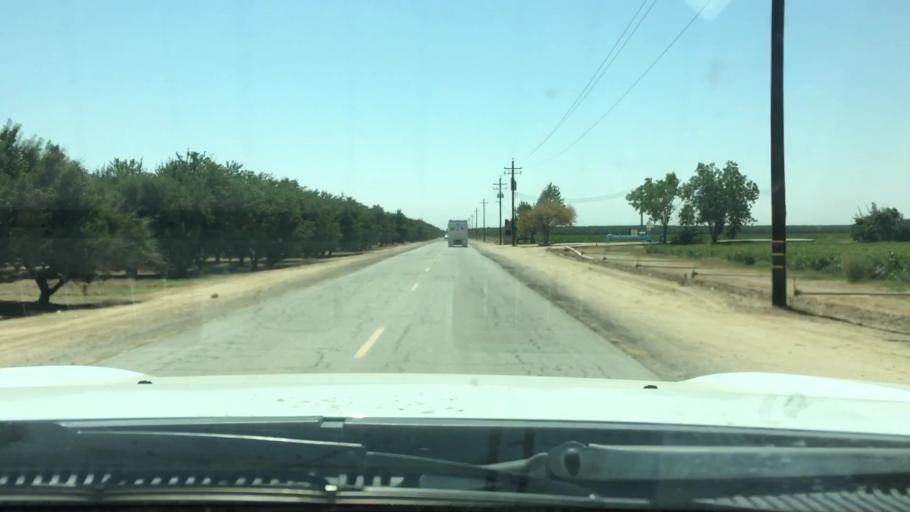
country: US
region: California
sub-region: Kern County
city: Wasco
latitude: 35.5068
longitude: -119.4034
